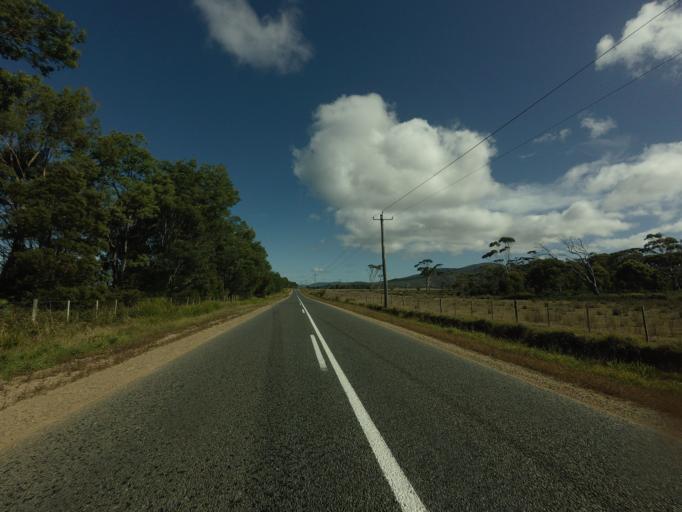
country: AU
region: Tasmania
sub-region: Break O'Day
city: St Helens
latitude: -41.7642
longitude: 148.2720
